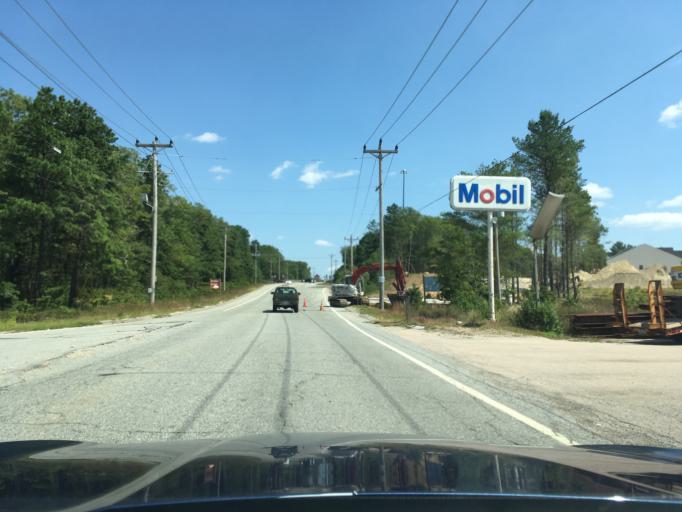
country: US
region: Rhode Island
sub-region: Kent County
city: West Warwick
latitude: 41.6569
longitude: -71.5511
